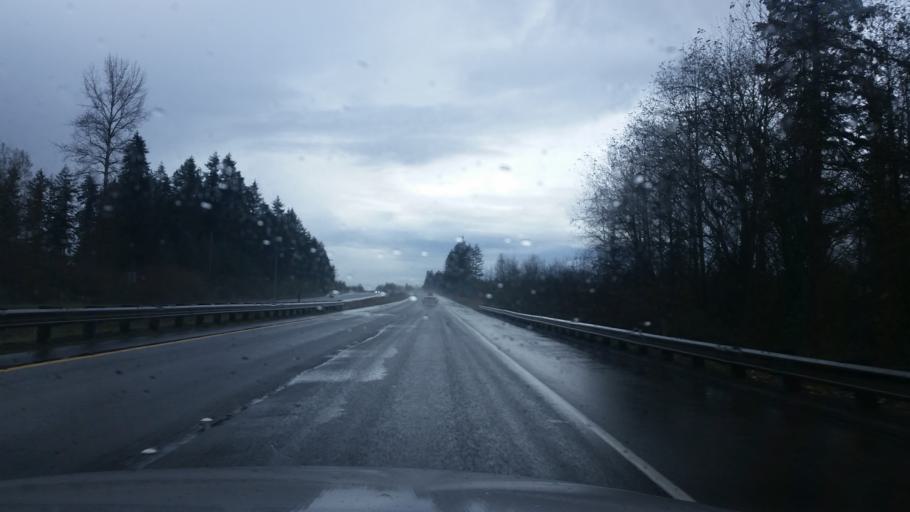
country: US
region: Washington
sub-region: King County
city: Maple Valley
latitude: 47.3776
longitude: -122.0813
